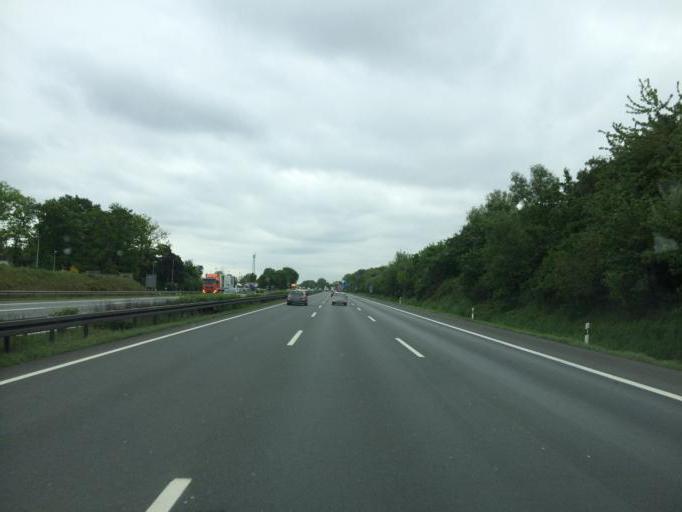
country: DE
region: Lower Saxony
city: Garbsen
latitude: 52.4213
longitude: 9.5504
